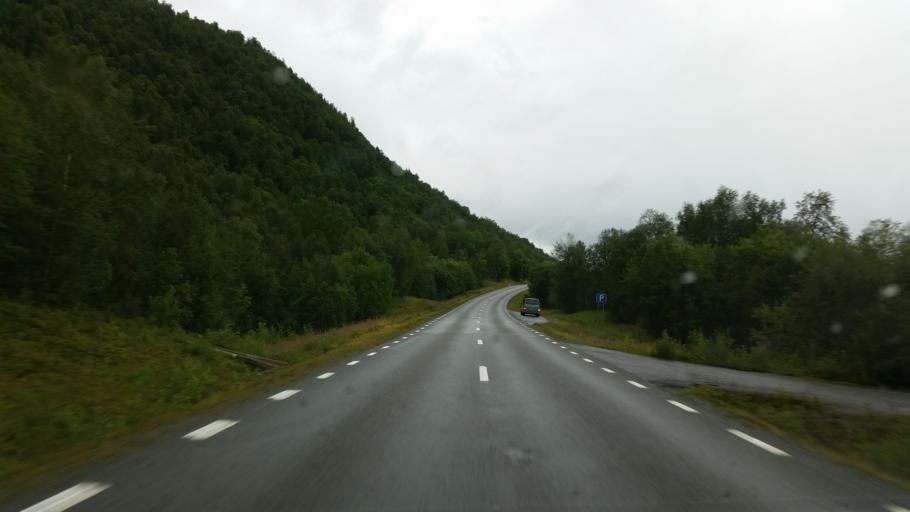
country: NO
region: Nordland
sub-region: Rana
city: Mo i Rana
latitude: 65.8758
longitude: 15.0049
